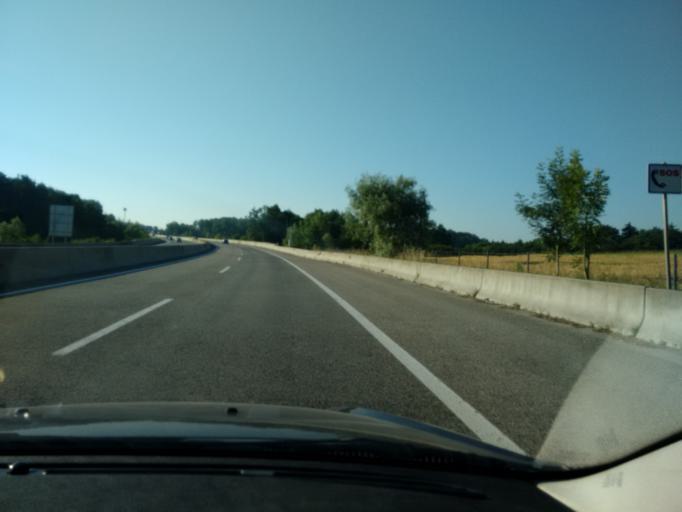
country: AT
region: Upper Austria
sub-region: Wels-Land
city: Sattledt
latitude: 48.0730
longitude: 14.0225
